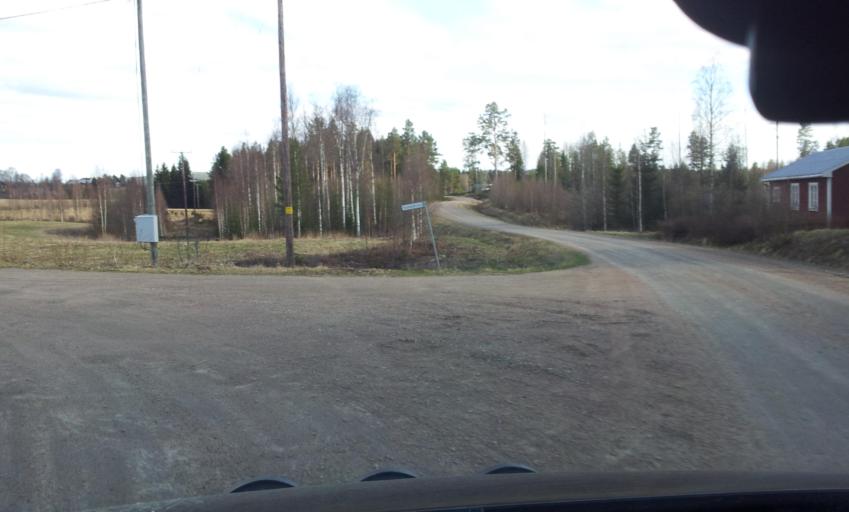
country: SE
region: Vaesternorrland
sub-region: Ange Kommun
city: Ange
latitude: 62.1509
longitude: 15.6598
